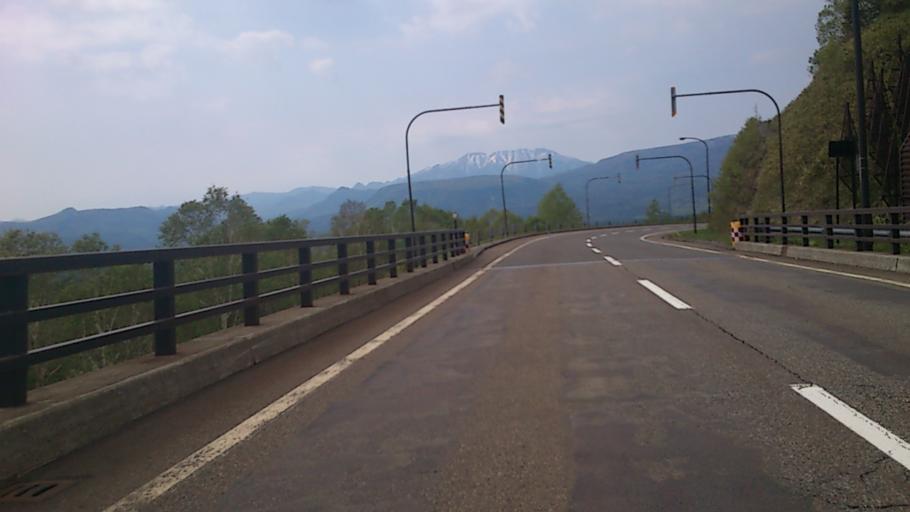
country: JP
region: Hokkaido
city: Kamikawa
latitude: 43.5769
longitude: 143.1261
